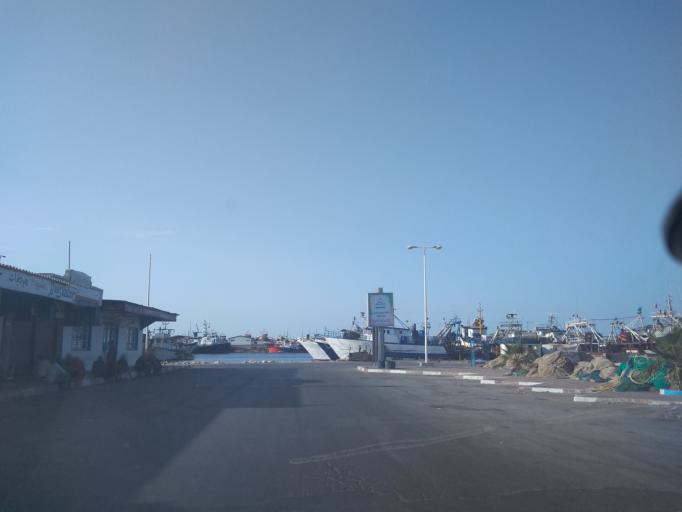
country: TN
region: Safaqis
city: Sfax
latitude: 34.7151
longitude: 10.7648
